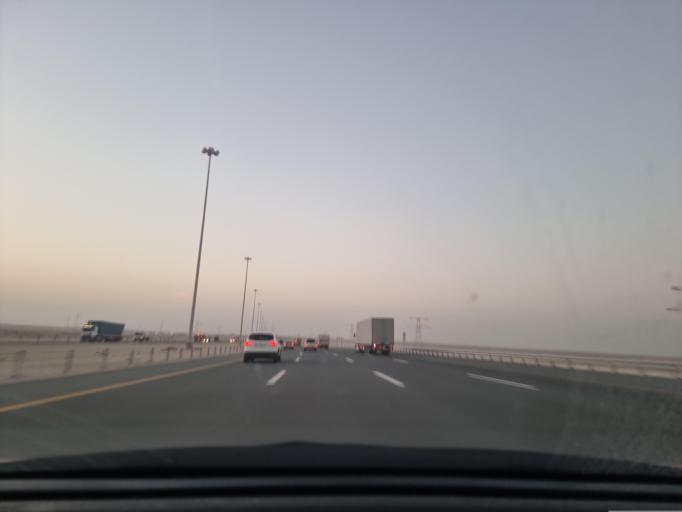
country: AE
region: Abu Dhabi
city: Abu Dhabi
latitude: 24.4350
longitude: 54.7638
